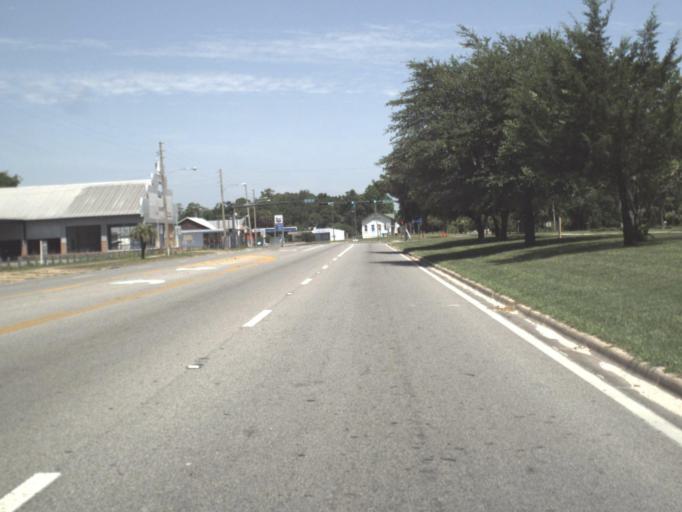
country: US
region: Florida
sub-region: Dixie County
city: Cross City
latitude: 29.6354
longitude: -83.1262
